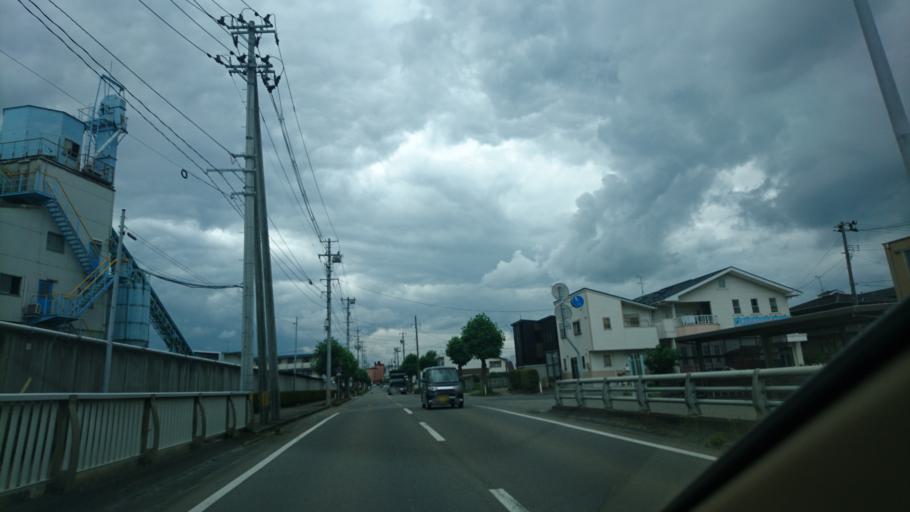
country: JP
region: Iwate
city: Kitakami
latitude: 39.2779
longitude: 141.1184
